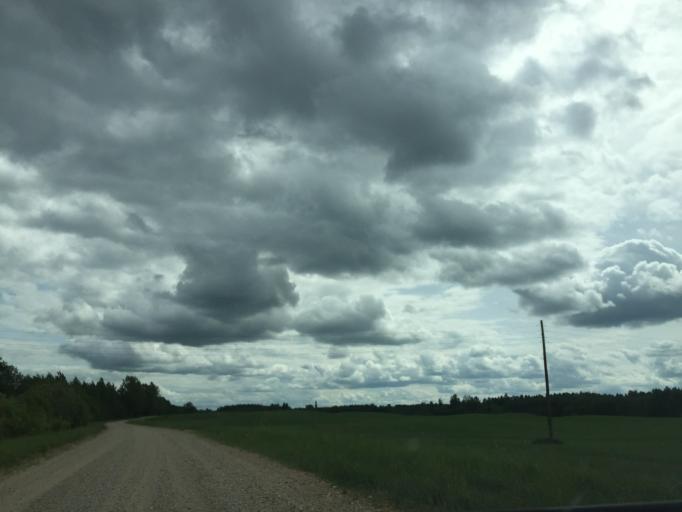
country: LV
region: Dagda
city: Dagda
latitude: 56.0601
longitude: 27.6482
